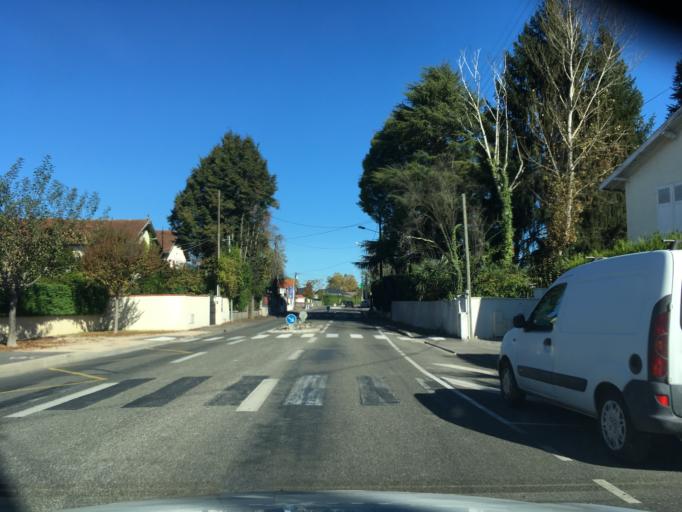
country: FR
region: Aquitaine
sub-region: Departement des Pyrenees-Atlantiques
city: Idron
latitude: 43.3004
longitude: -0.3320
